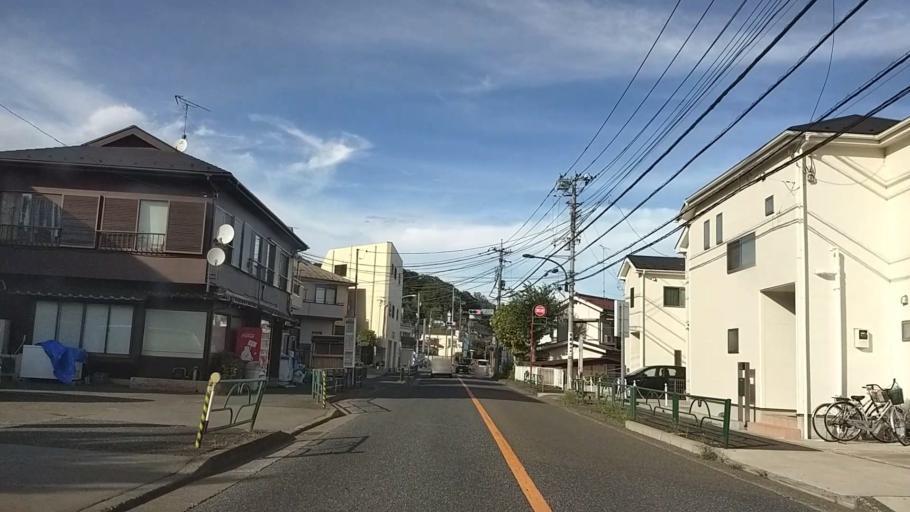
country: JP
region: Tokyo
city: Hachioji
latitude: 35.6376
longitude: 139.3178
